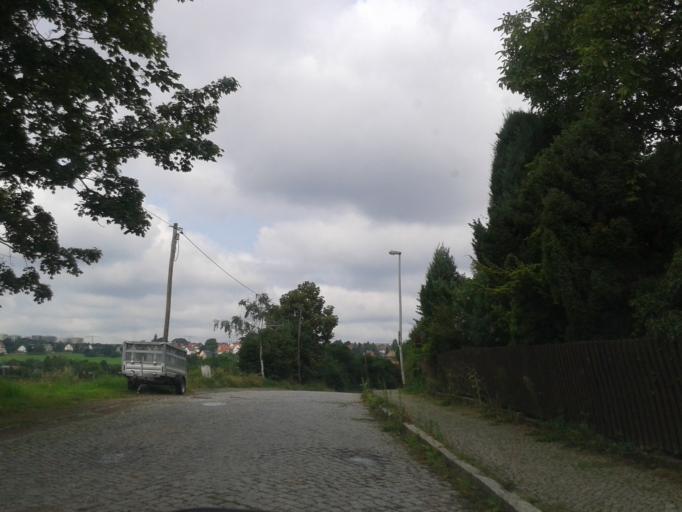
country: DE
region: Saxony
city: Bannewitz
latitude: 51.0118
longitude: 13.7432
